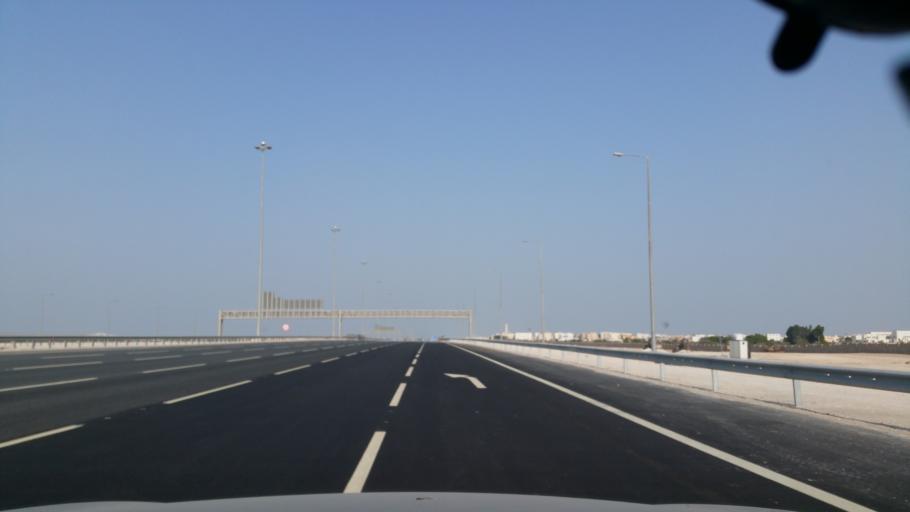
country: QA
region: Baladiyat Umm Salal
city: Umm Salal `Ali
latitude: 25.4520
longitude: 51.4246
